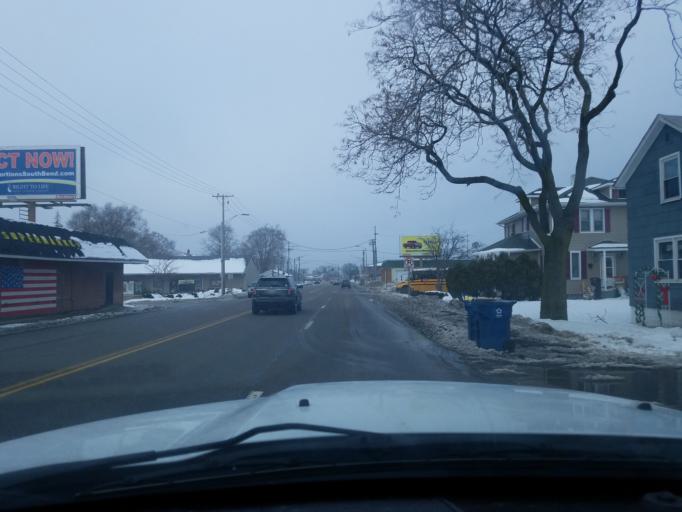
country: US
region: Indiana
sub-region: Saint Joseph County
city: Mishawaka
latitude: 41.6529
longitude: -86.1768
